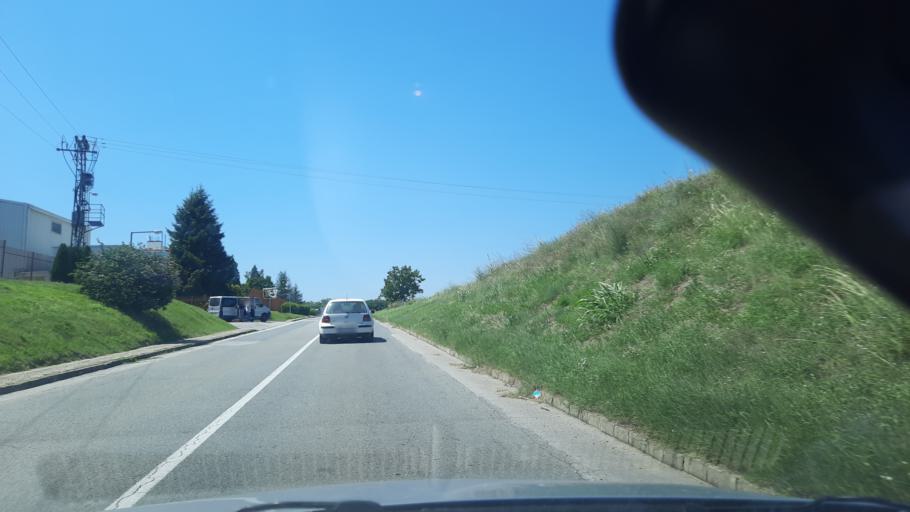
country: RS
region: Central Serbia
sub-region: Branicevski Okrug
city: Pozarevac
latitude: 44.7958
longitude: 21.1975
